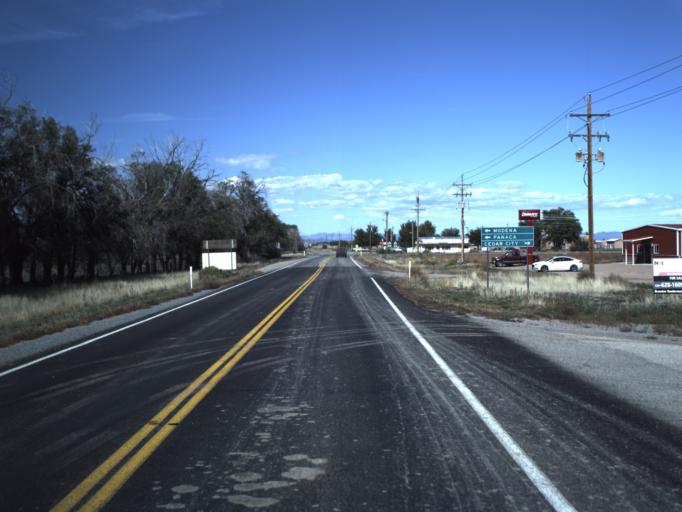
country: US
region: Utah
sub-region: Washington County
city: Enterprise
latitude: 37.7075
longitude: -113.6563
